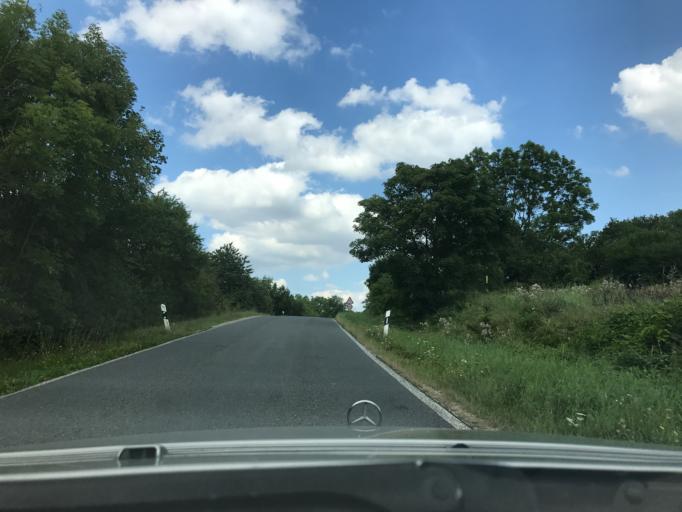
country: DE
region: Thuringia
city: Sollstedt
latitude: 51.2572
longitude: 10.4775
